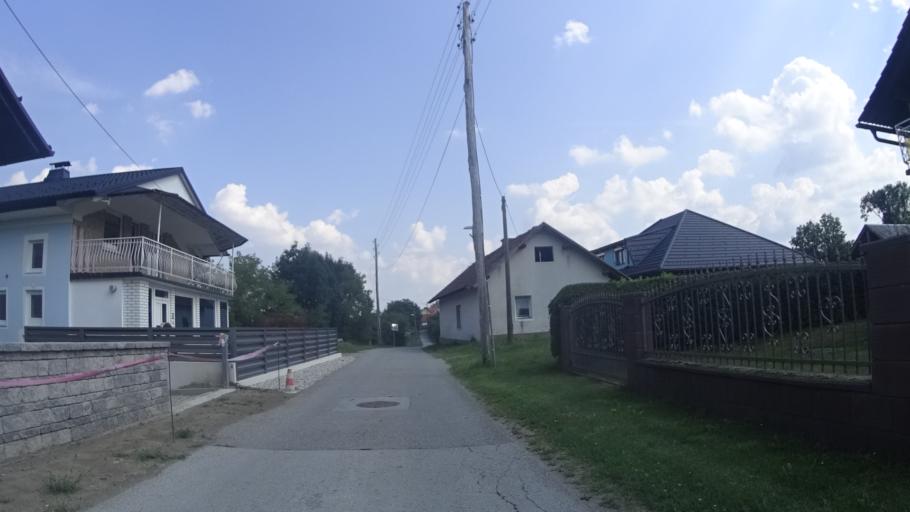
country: SI
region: Kidricevo
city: Kidricevo
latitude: 46.4428
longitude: 15.8091
